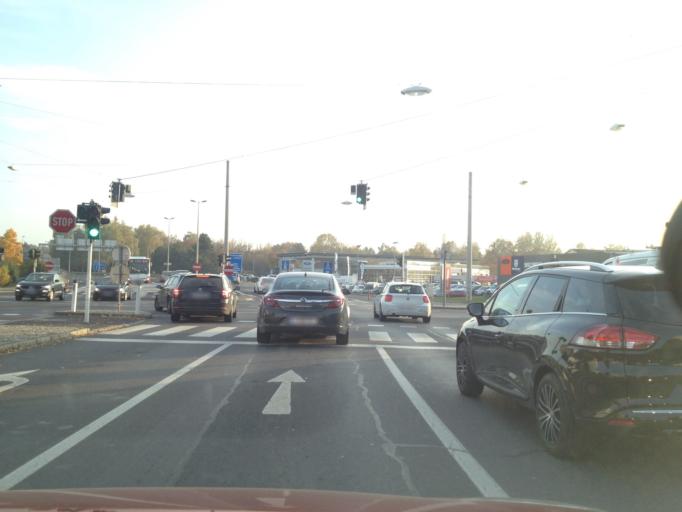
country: AT
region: Upper Austria
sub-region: Linz Stadt
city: Linz
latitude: 48.3299
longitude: 14.3177
